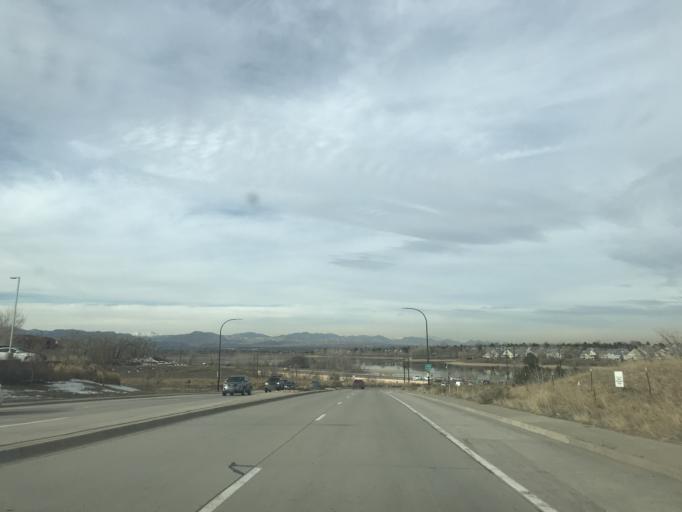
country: US
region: Colorado
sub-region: Douglas County
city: Highlands Ranch
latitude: 39.5632
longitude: -105.0091
